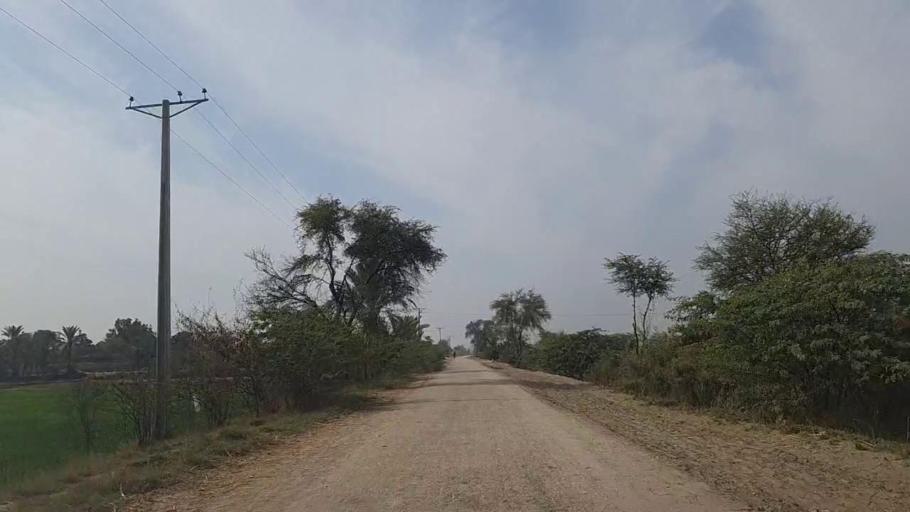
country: PK
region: Sindh
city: Daur
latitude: 26.4516
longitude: 68.4235
